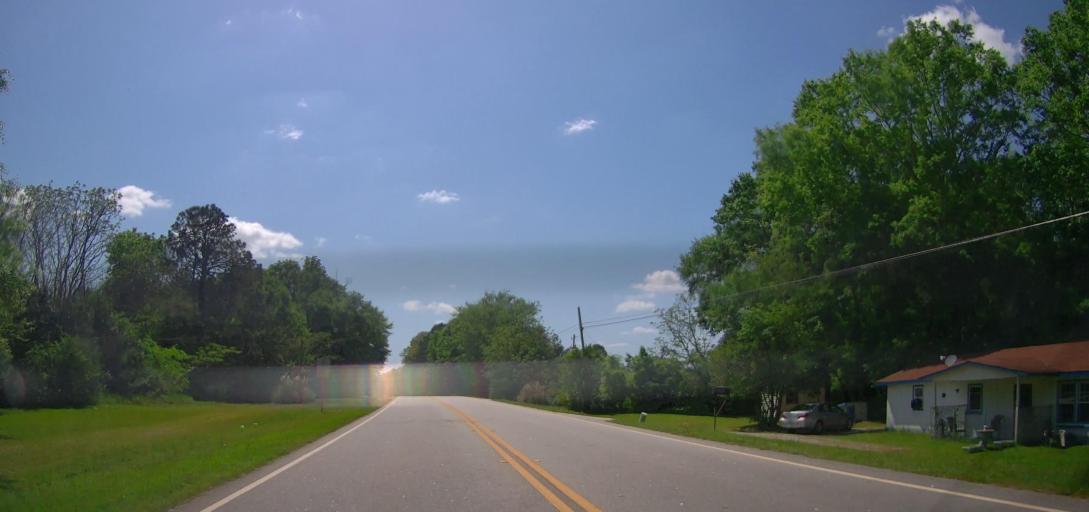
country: US
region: Georgia
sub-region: Putnam County
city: Eatonton
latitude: 33.3396
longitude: -83.3584
